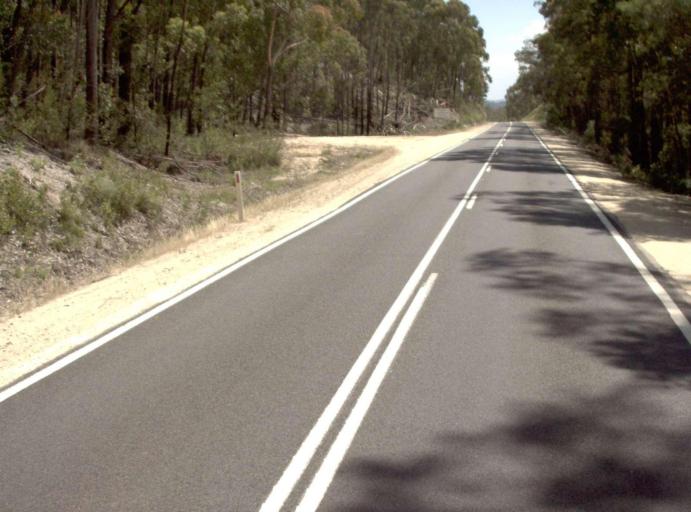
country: AU
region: New South Wales
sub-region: Bombala
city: Bombala
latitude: -37.5640
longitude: 149.2416
